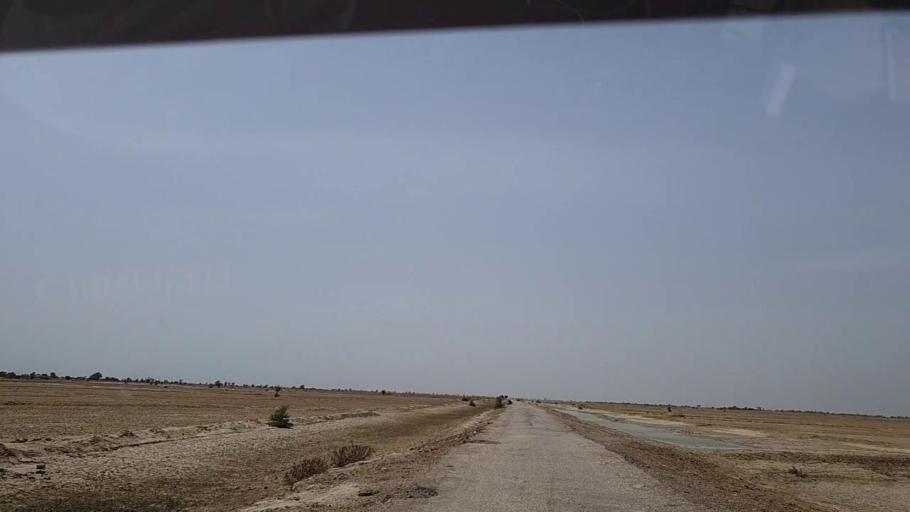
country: PK
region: Sindh
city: Johi
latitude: 26.7218
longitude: 67.6445
